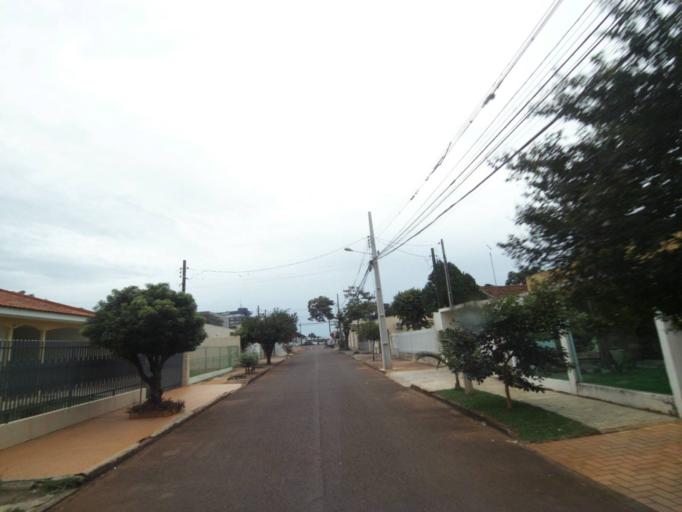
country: BR
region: Parana
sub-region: Campo Mourao
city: Campo Mourao
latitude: -24.0280
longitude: -52.3626
